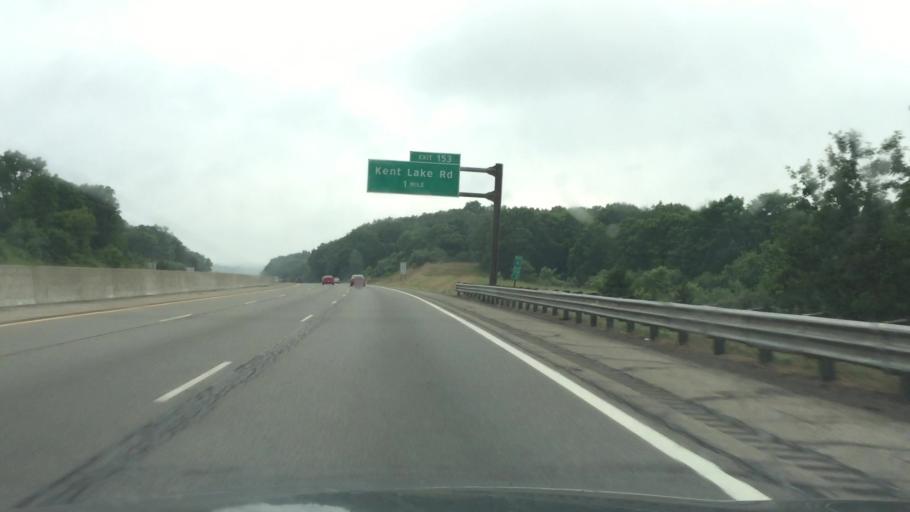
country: US
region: Michigan
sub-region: Oakland County
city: South Lyon
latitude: 42.5216
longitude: -83.6310
